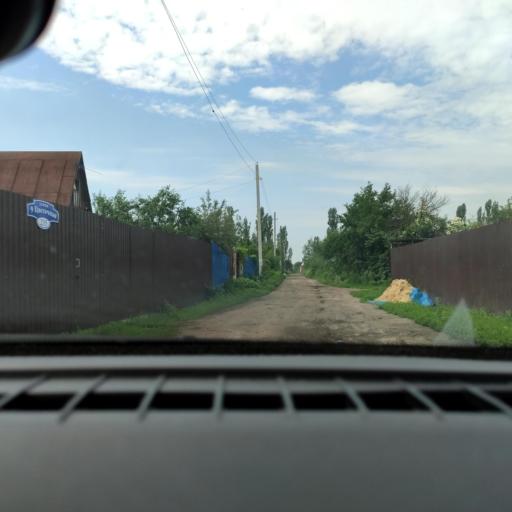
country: RU
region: Voronezj
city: Maslovka
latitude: 51.5026
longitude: 39.1991
